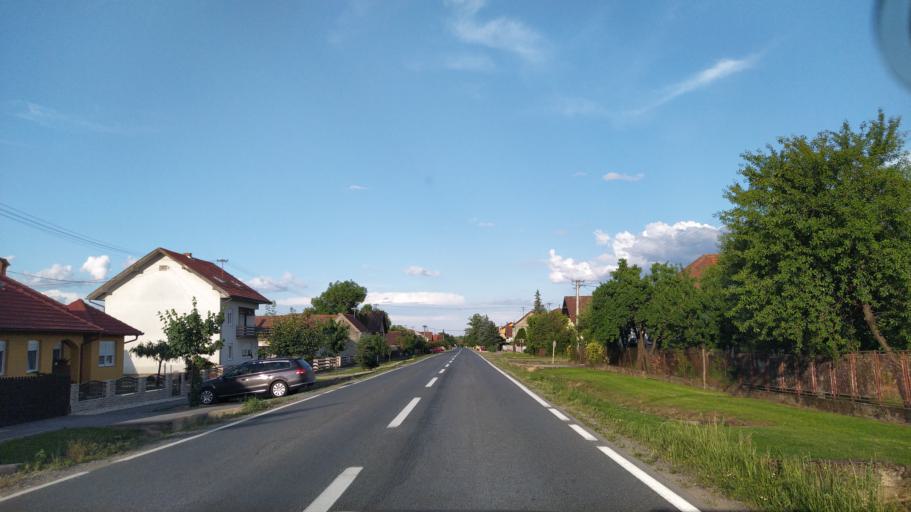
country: HR
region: Virovitick-Podravska
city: Cacinci
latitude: 45.5997
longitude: 17.8511
